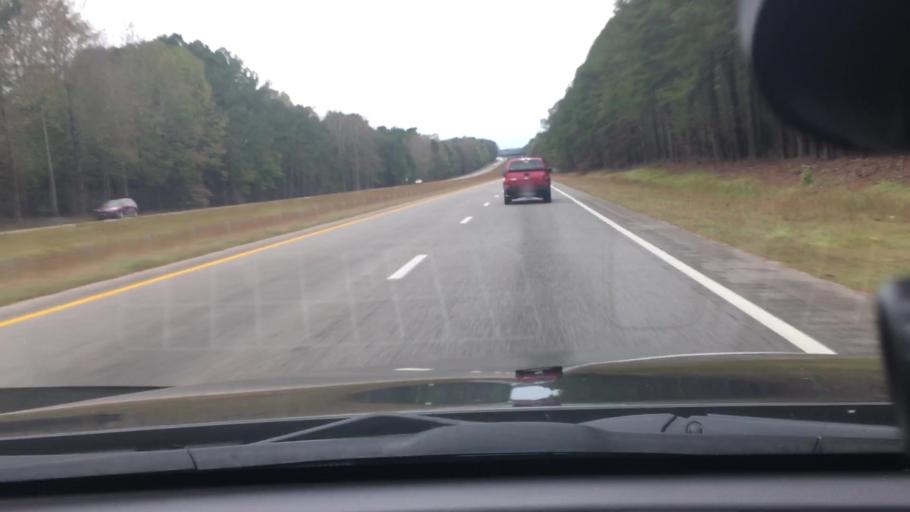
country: US
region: North Carolina
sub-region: Wake County
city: Zebulon
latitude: 35.8110
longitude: -78.2267
